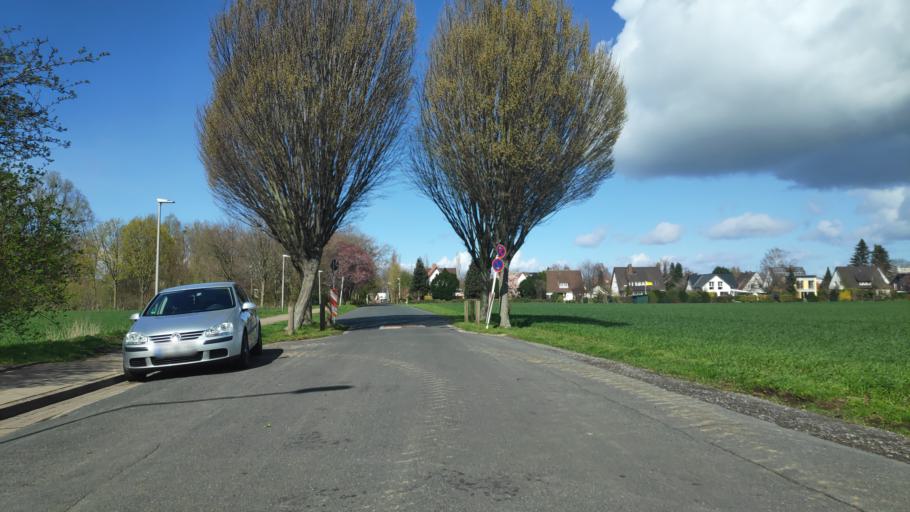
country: DE
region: North Rhine-Westphalia
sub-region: Regierungsbezirk Detmold
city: Minden
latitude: 52.2936
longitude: 8.8950
